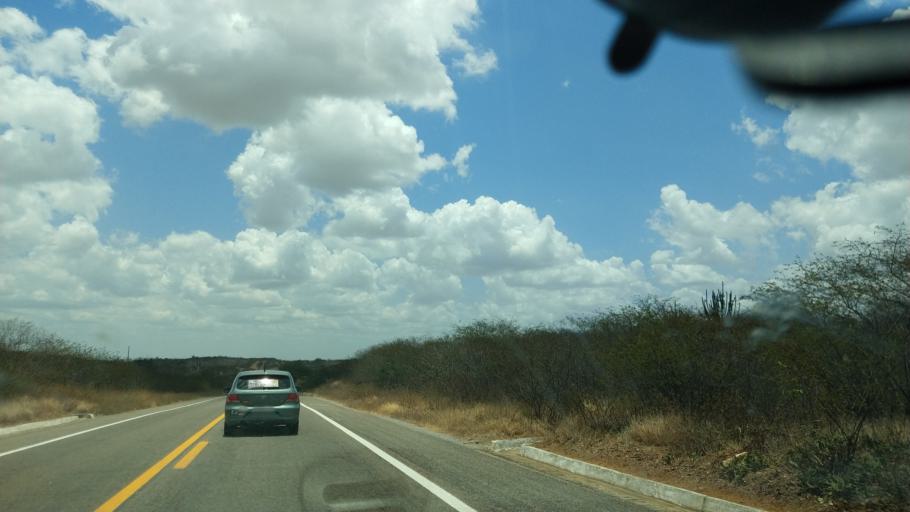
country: BR
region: Rio Grande do Norte
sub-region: Cerro Cora
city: Cerro Cora
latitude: -6.2093
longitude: -36.2933
